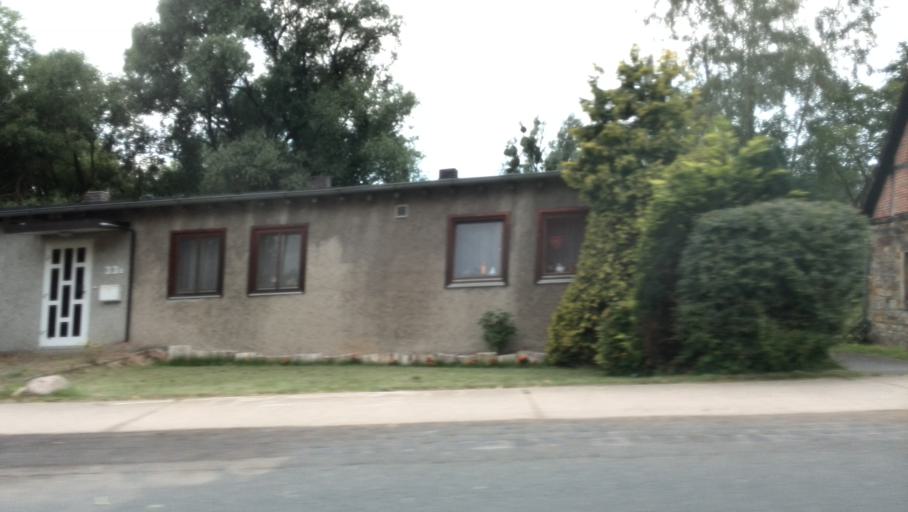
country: DE
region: Lower Saxony
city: Holle
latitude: 52.1031
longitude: 10.1226
